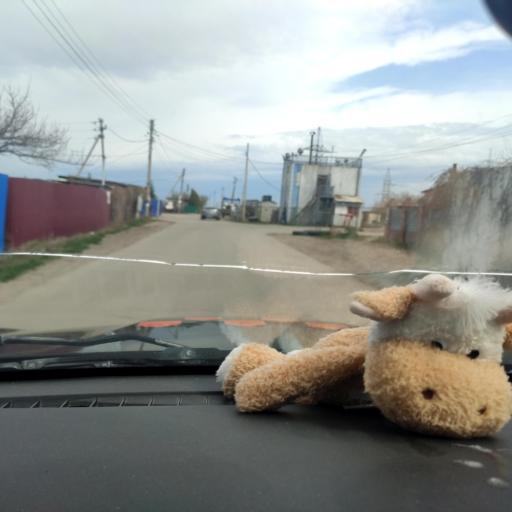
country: RU
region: Samara
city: Tol'yatti
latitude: 53.5946
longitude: 49.2432
